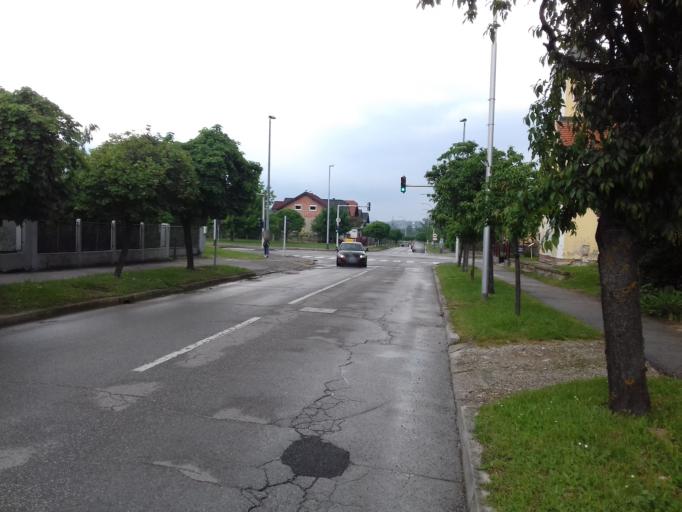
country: HR
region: Varazdinska
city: Ivanec
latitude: 46.2284
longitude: 16.1240
